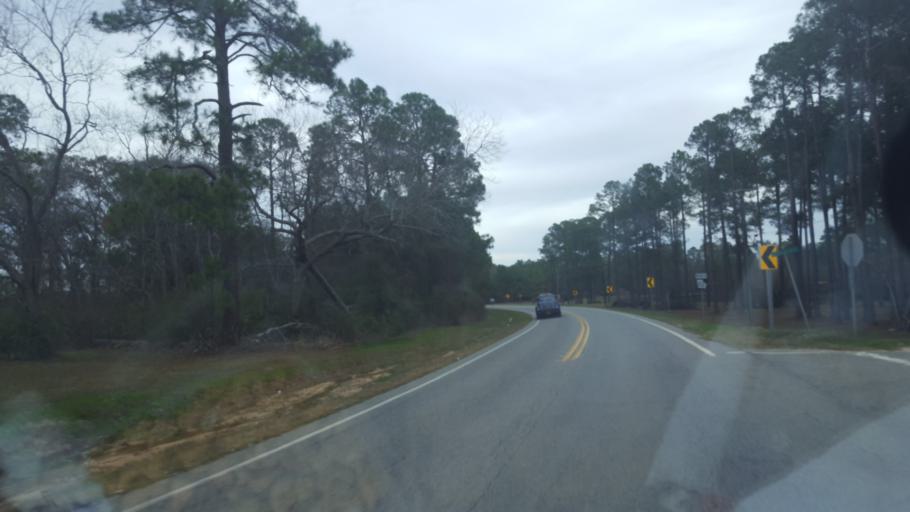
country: US
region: Georgia
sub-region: Turner County
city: Ashburn
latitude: 31.7237
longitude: -83.5833
